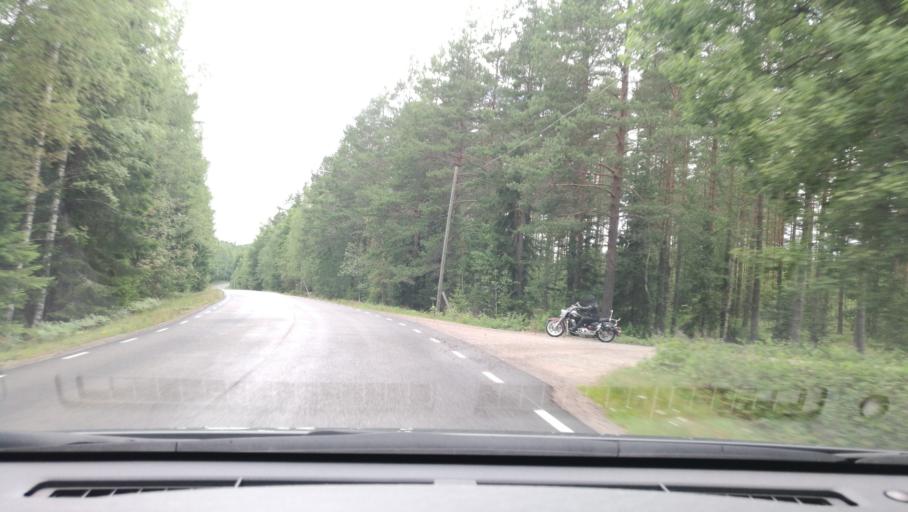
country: SE
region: OEstergoetland
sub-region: Norrkopings Kommun
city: Svartinge
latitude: 58.8186
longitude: 16.0221
